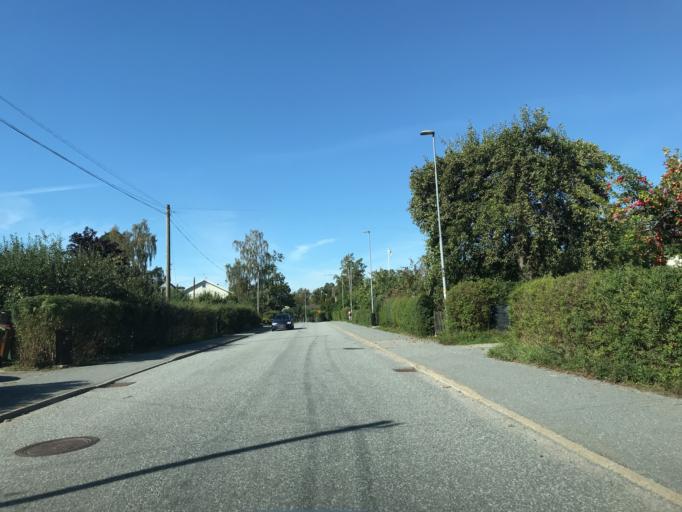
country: SE
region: Stockholm
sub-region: Sollentuna Kommun
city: Sollentuna
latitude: 59.4216
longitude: 17.9334
